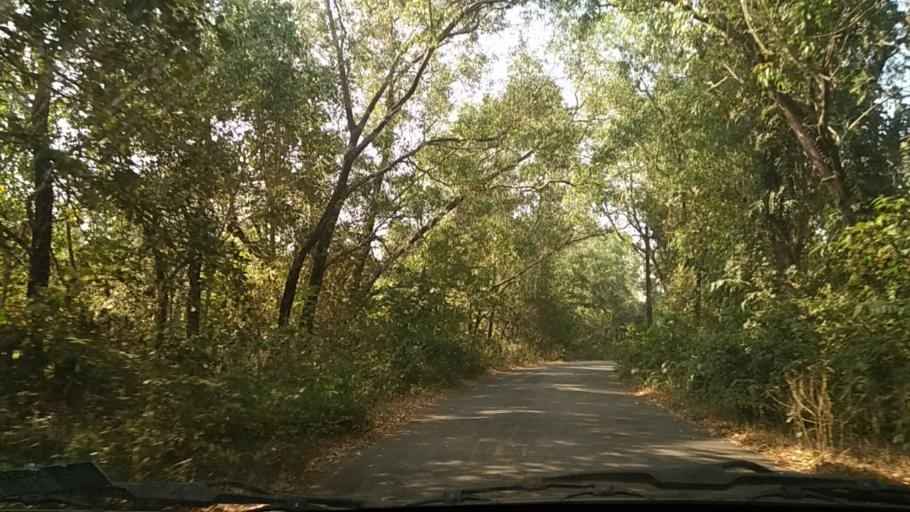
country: IN
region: Goa
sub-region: North Goa
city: Ponda
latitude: 15.3651
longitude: 74.0872
